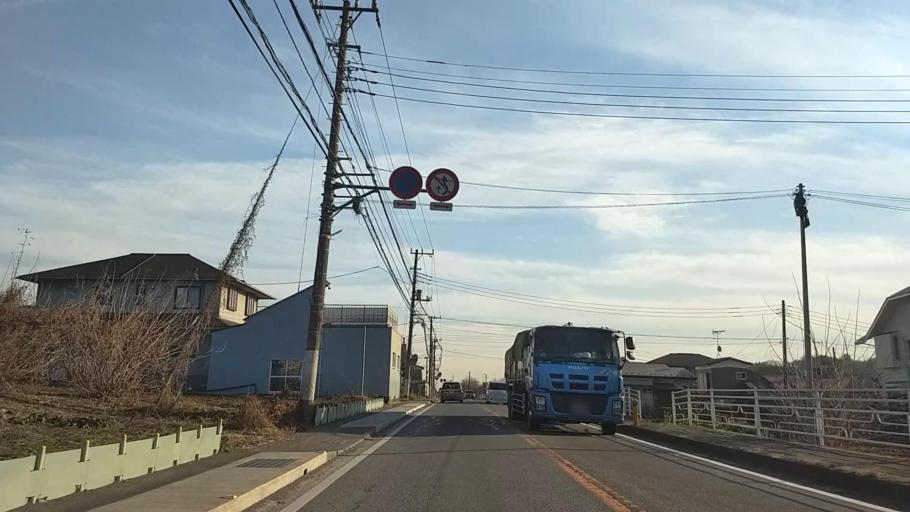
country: JP
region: Kanagawa
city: Zama
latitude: 35.5042
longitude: 139.3102
